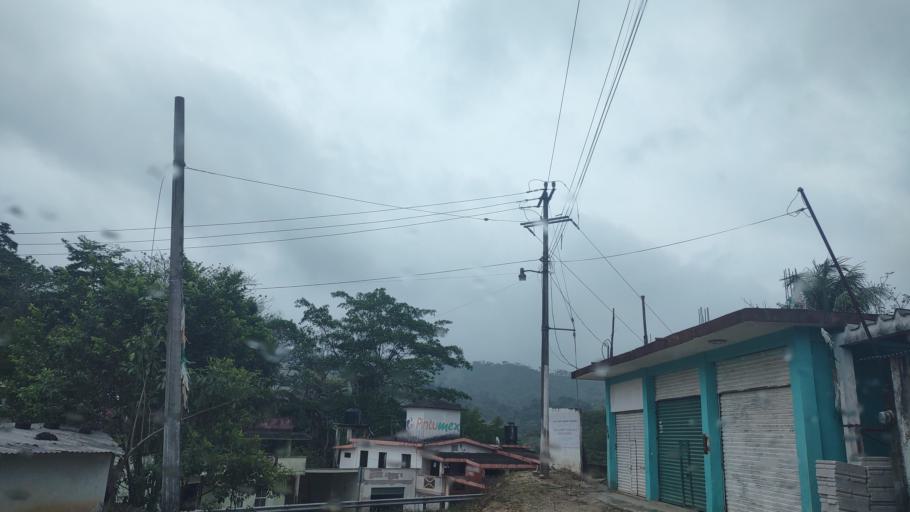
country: MX
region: Veracruz
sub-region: Uxpanapa
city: Poblado 10
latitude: 17.4511
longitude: -94.0966
